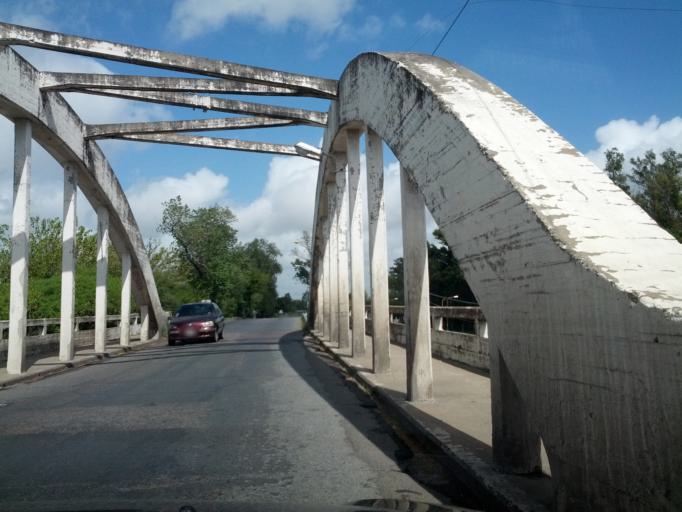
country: AR
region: Buenos Aires
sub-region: Partido de Lujan
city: Lujan
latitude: -34.5771
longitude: -59.0893
